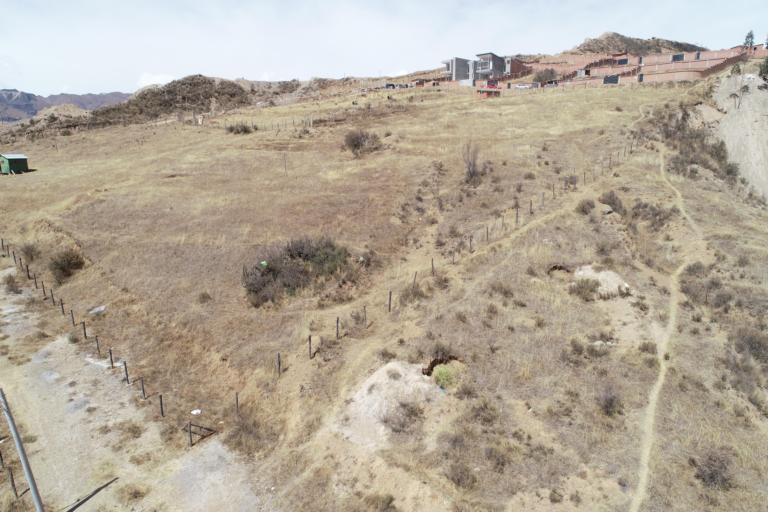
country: BO
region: La Paz
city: La Paz
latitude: -16.5518
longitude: -68.0637
